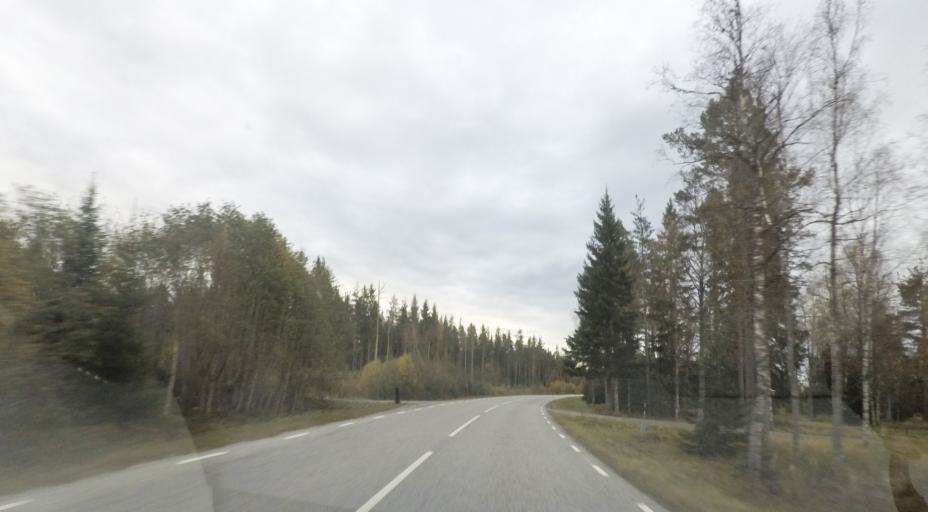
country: SE
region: OErebro
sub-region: Hallefors Kommun
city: Haellefors
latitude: 59.7980
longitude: 14.5092
